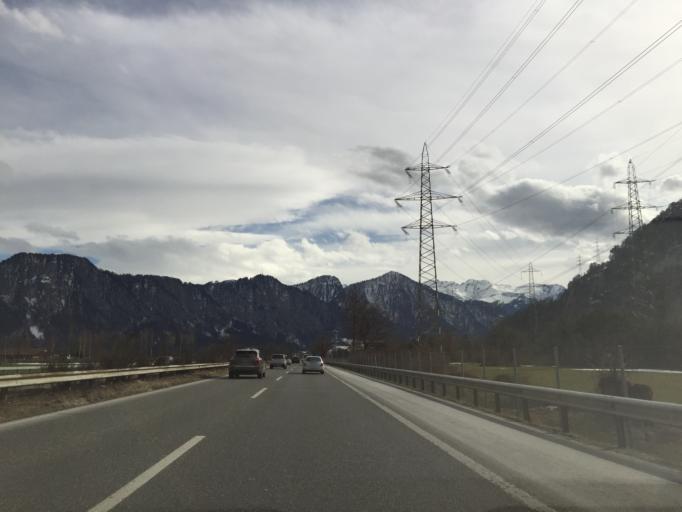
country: CH
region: Grisons
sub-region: Landquart District
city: Maienfeld
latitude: 46.9855
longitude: 9.5389
